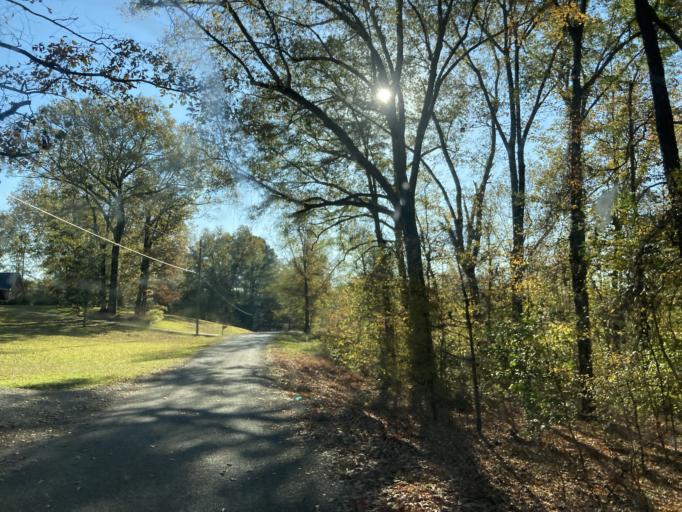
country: US
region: Mississippi
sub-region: Yazoo County
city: Yazoo City
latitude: 32.7929
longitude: -90.3556
